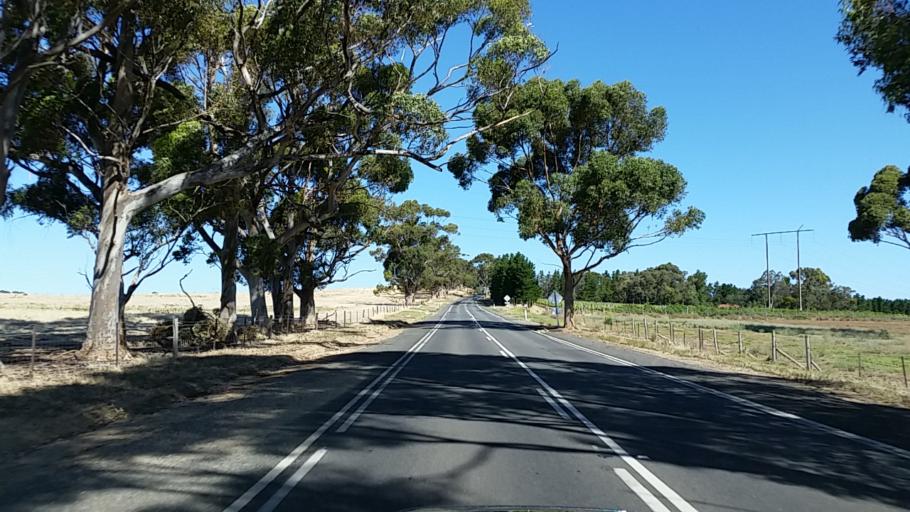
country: AU
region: South Australia
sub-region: Playford
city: One Tree Hill
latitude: -34.7106
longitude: 138.7312
